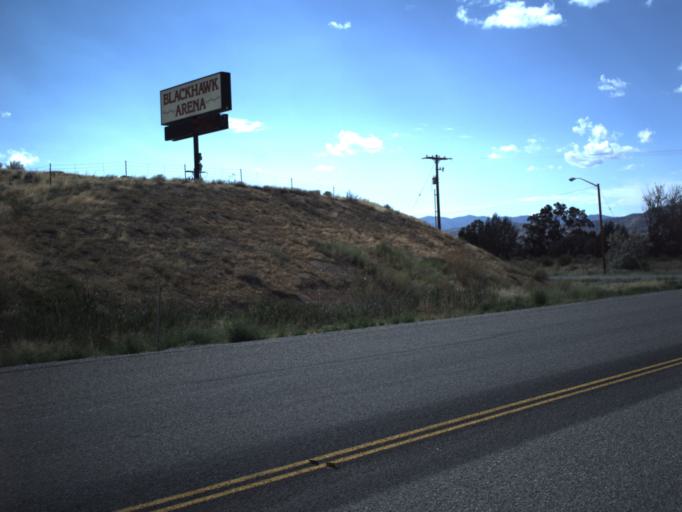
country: US
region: Utah
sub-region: Sevier County
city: Salina
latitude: 38.9482
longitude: -111.8584
